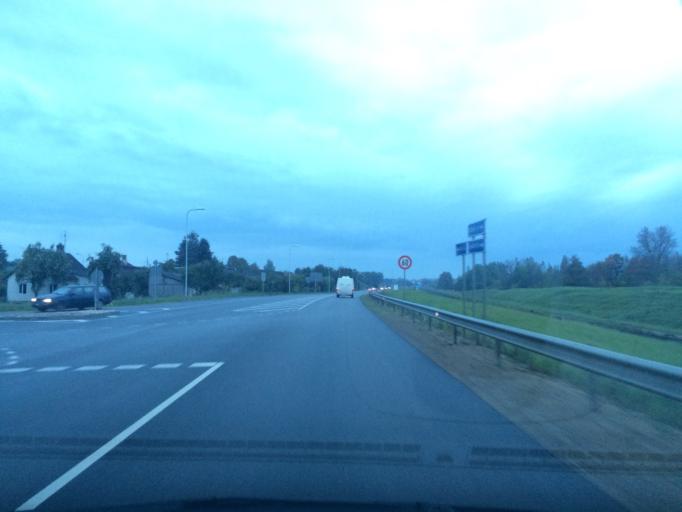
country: LV
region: Jekabpils Rajons
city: Jekabpils
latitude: 56.5076
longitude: 25.8791
